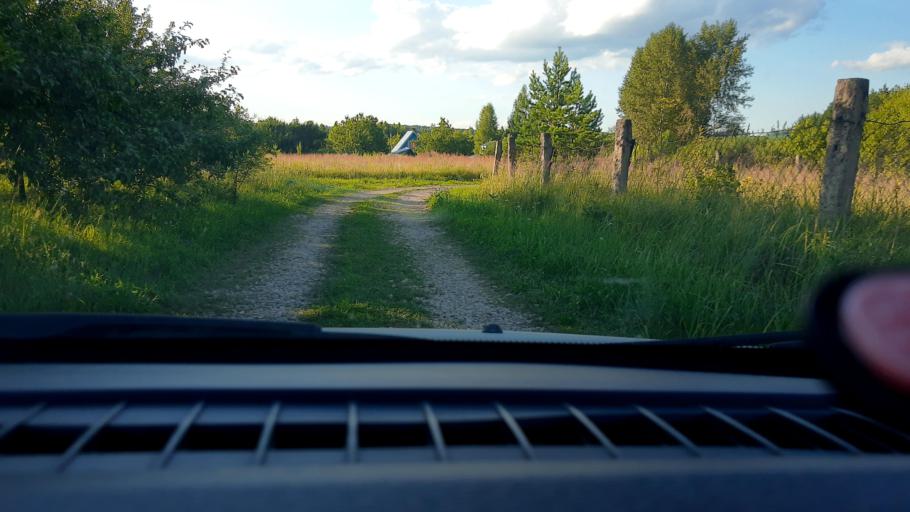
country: RU
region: Nizjnij Novgorod
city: Burevestnik
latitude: 56.0451
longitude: 43.8830
